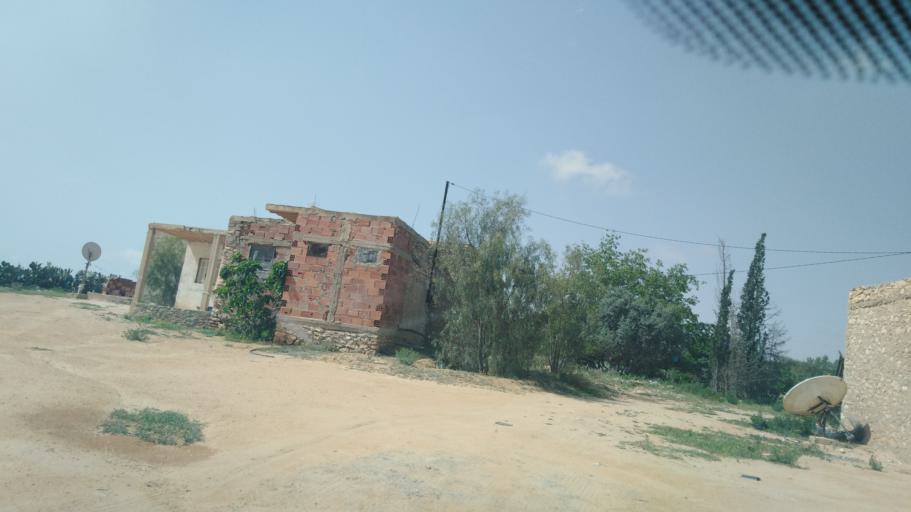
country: TN
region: Safaqis
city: Sfax
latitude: 34.7283
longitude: 10.5654
